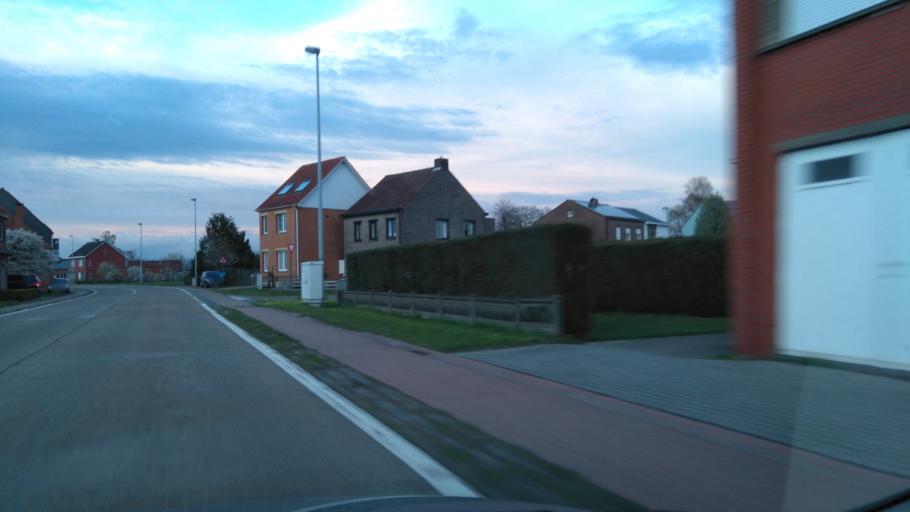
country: BE
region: Flanders
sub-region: Provincie Antwerpen
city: Oud-Turnhout
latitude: 51.3104
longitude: 4.9783
